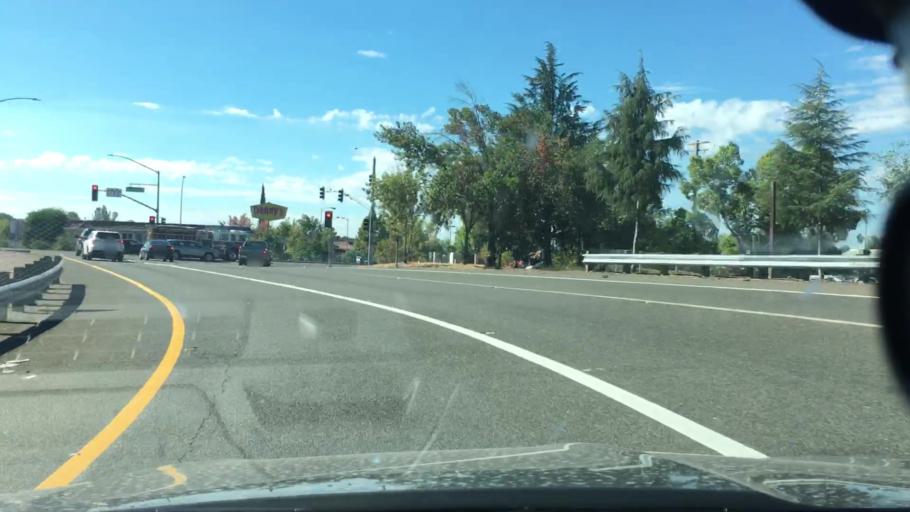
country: US
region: California
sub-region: Sacramento County
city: Foothill Farms
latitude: 38.6618
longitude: -121.3618
